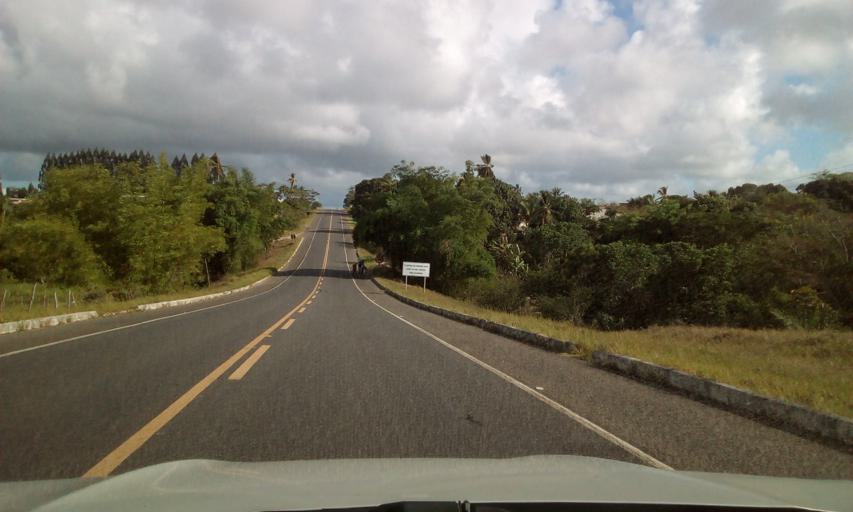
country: BR
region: Bahia
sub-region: Conde
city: Conde
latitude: -11.8315
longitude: -37.6354
